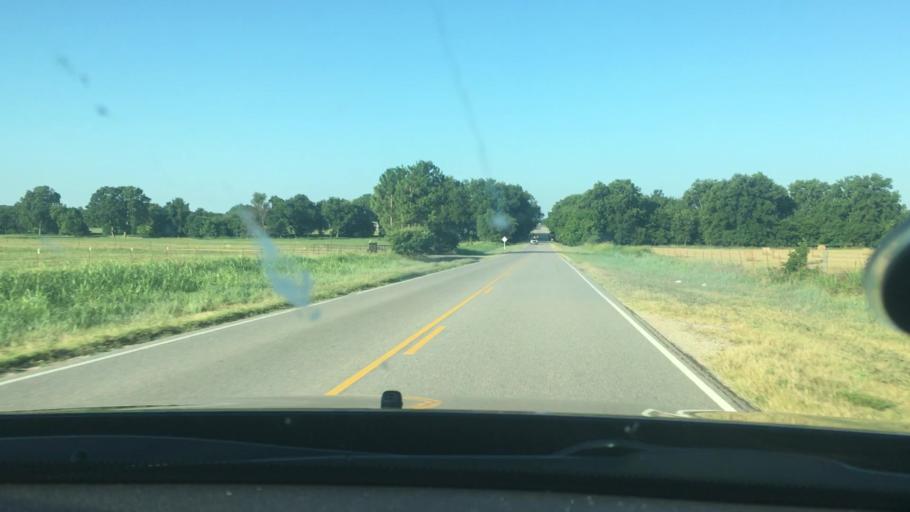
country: US
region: Oklahoma
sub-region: Pontotoc County
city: Ada
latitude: 34.6484
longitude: -96.7982
